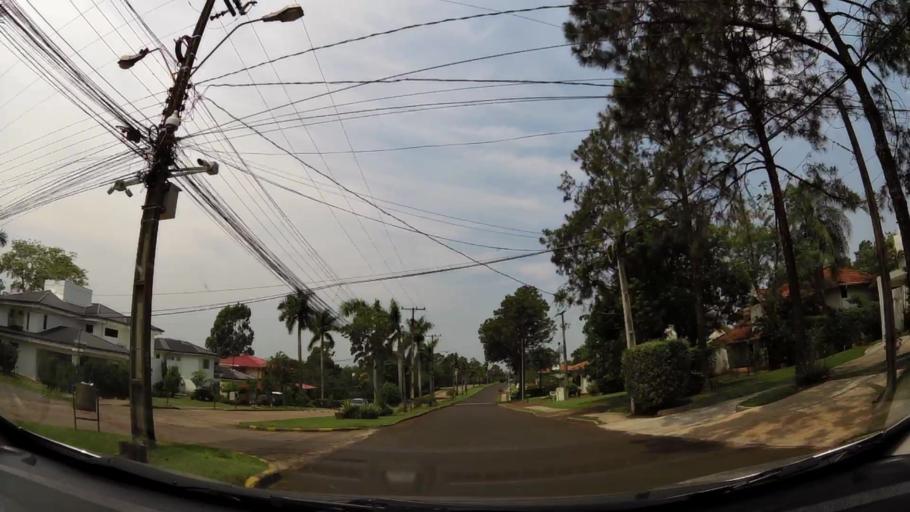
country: PY
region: Alto Parana
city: Ciudad del Este
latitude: -25.4907
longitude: -54.6137
